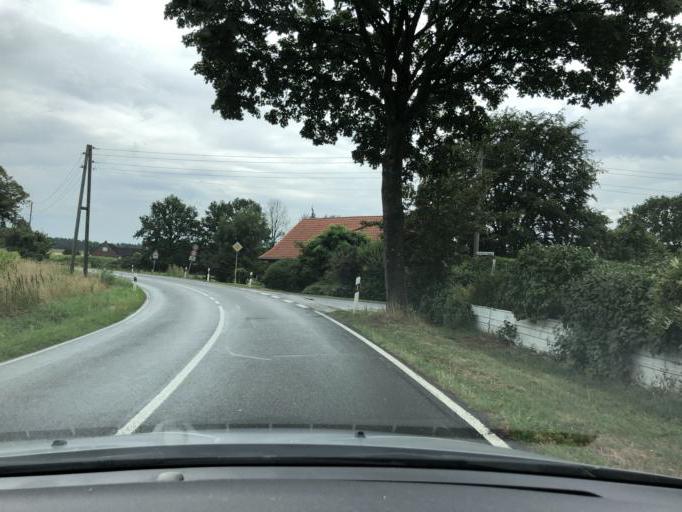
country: DE
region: North Rhine-Westphalia
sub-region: Regierungsbezirk Dusseldorf
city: Schermbeck
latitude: 51.6466
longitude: 6.8940
